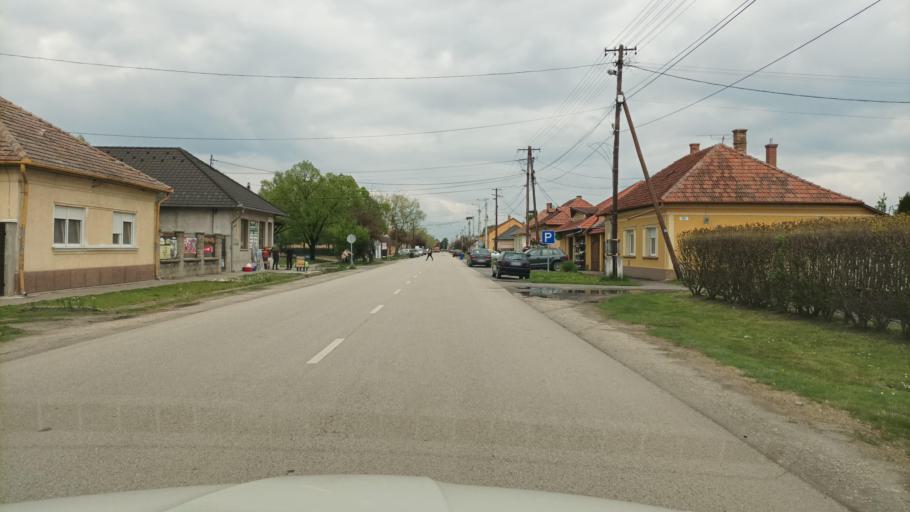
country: HU
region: Pest
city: Tortel
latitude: 47.1195
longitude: 19.9331
